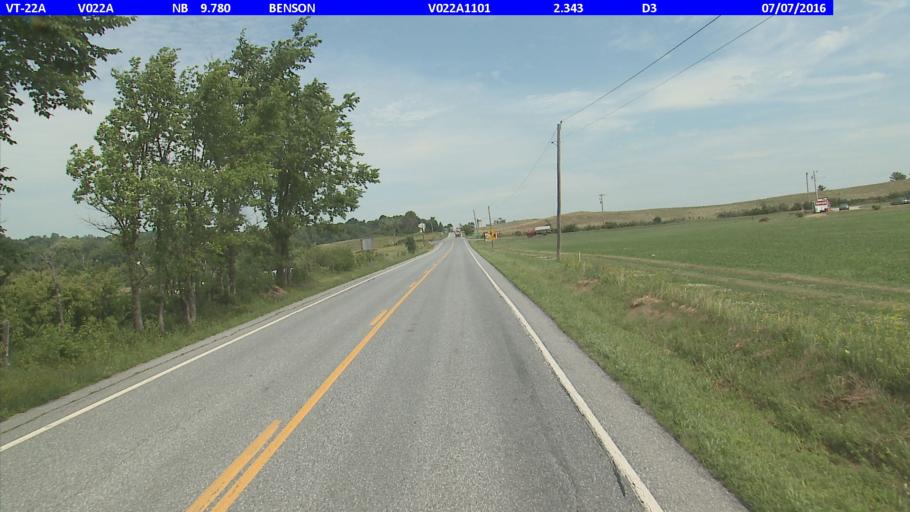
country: US
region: Vermont
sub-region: Rutland County
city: Fair Haven
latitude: 43.7023
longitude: -73.2955
